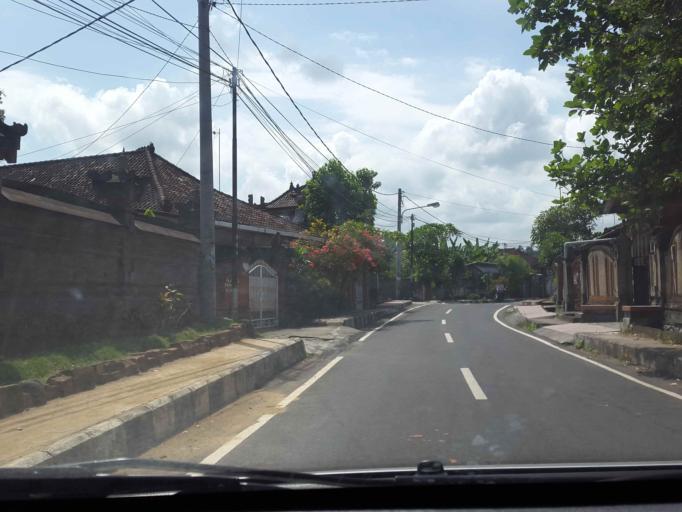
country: ID
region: Bali
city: Klungkung
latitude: -8.5267
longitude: 115.3996
